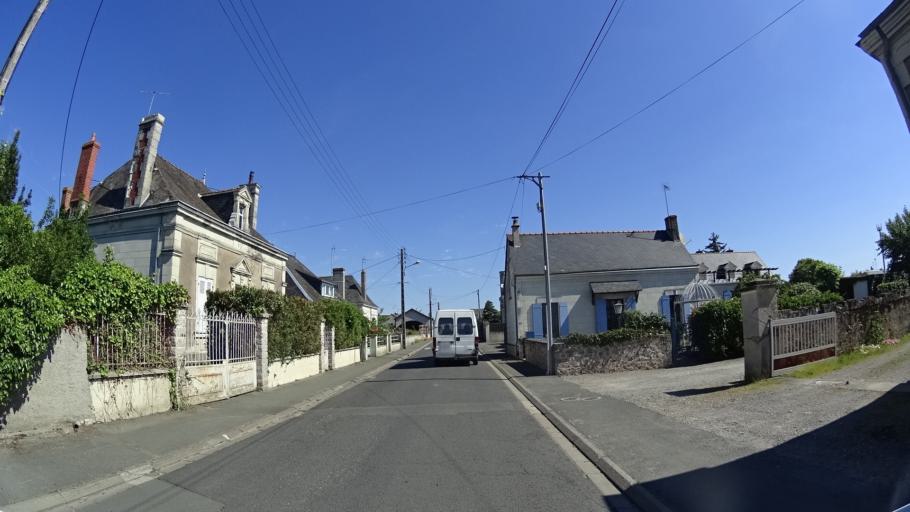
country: FR
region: Pays de la Loire
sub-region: Departement de Maine-et-Loire
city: Saint-Mathurin-sur-Loire
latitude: 47.4132
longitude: -0.3187
